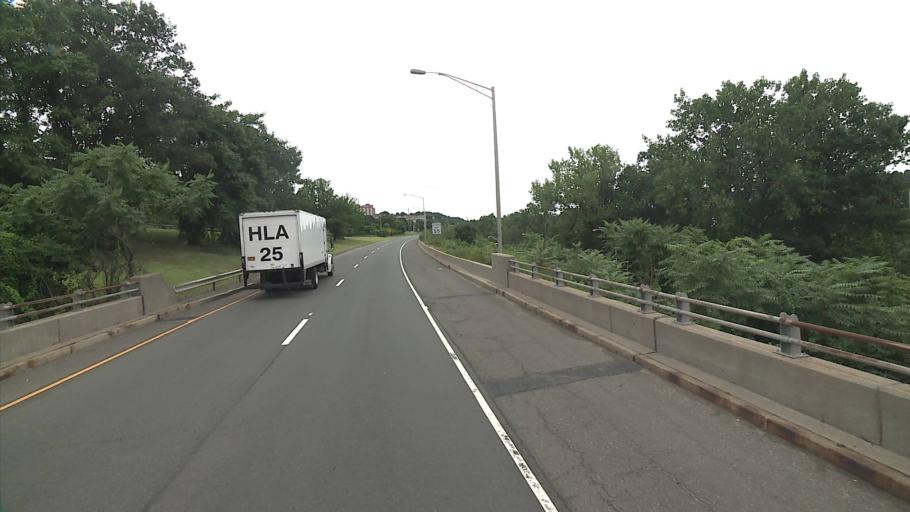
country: US
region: Connecticut
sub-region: New Haven County
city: Waterbury
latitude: 41.5527
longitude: -73.0530
